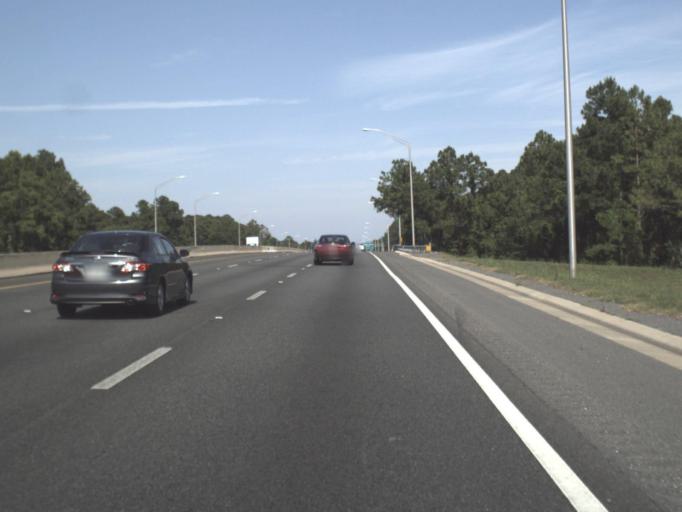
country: US
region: Florida
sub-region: Saint Johns County
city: Ponte Vedra Beach
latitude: 30.2511
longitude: -81.4855
